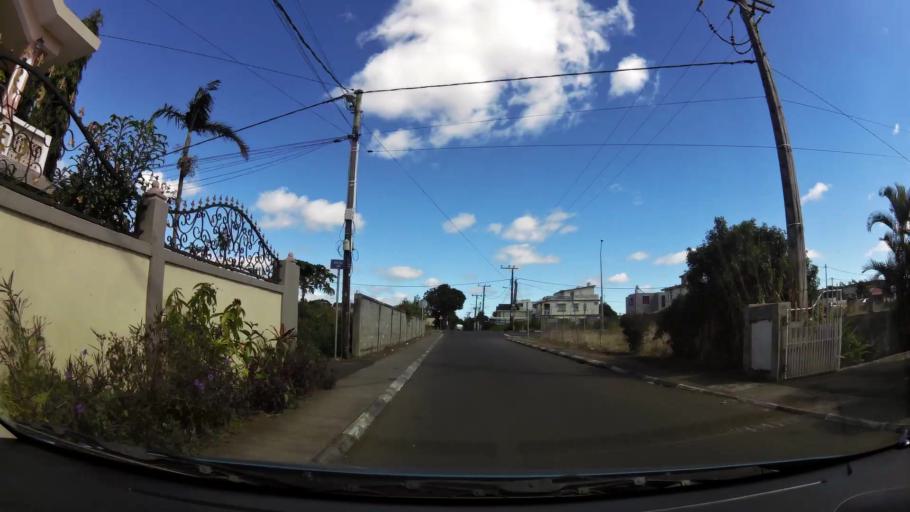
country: MU
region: Plaines Wilhems
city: Vacoas
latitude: -20.2877
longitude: 57.4779
